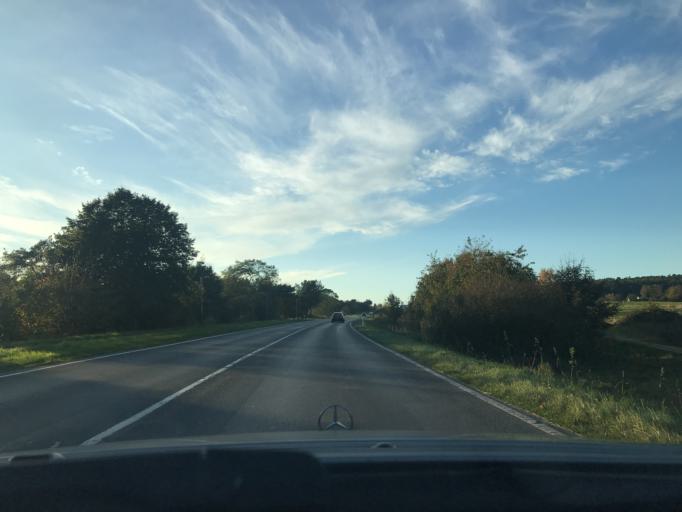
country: DE
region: Mecklenburg-Vorpommern
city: Seebad Bansin
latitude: 53.9615
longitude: 14.1430
